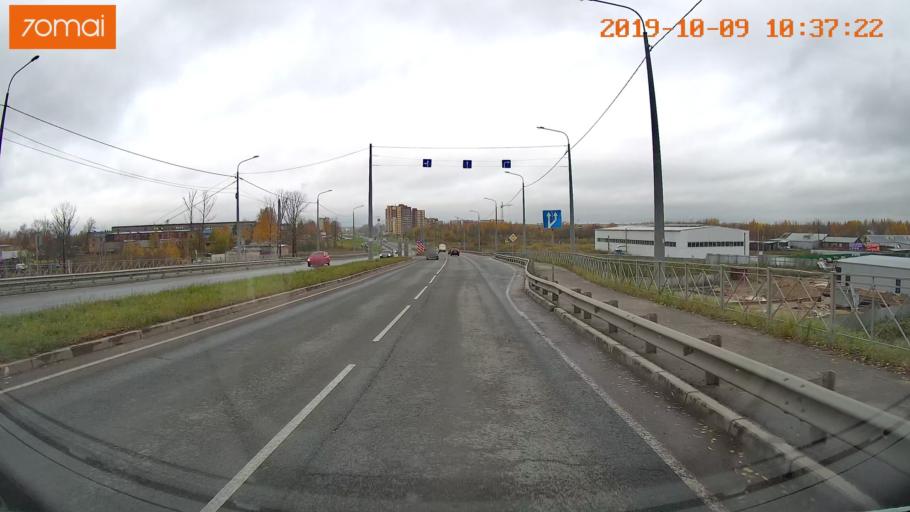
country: RU
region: Vologda
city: Vologda
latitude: 59.2346
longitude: 39.8638
